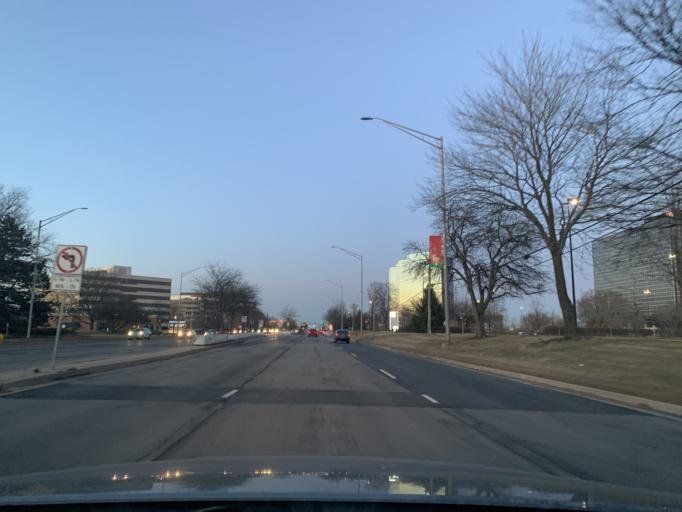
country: US
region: Illinois
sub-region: Cook County
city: Hoffman Estates
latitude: 42.0399
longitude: -88.0453
